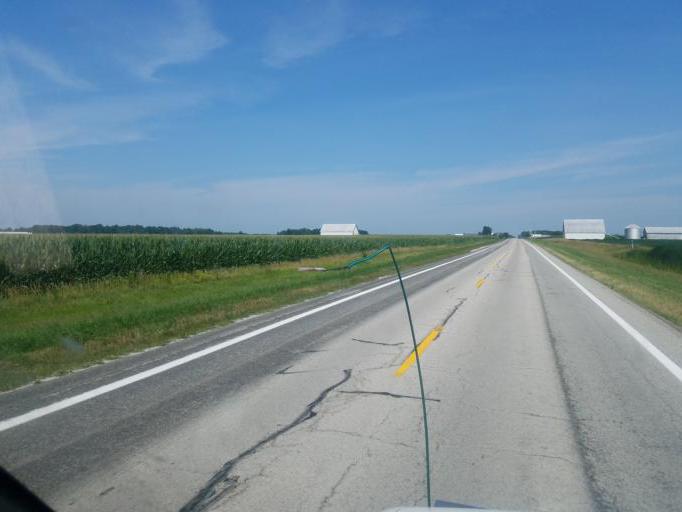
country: US
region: Ohio
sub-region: Auglaize County
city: Saint Marys
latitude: 40.4950
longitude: -84.4268
